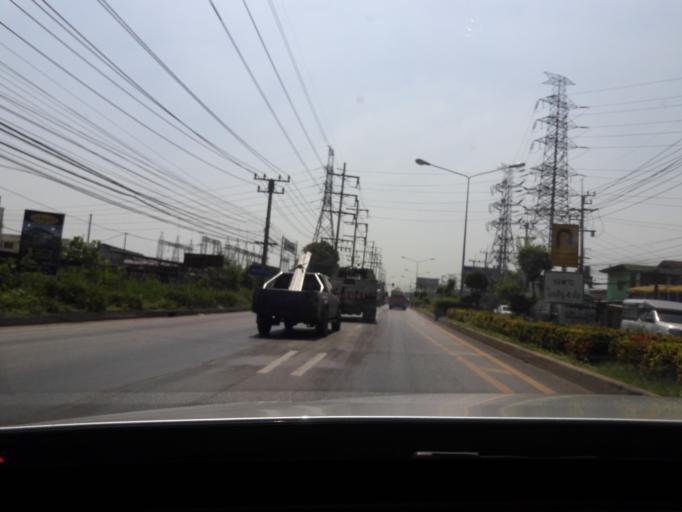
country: TH
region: Samut Sakhon
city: Samut Sakhon
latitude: 13.5947
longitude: 100.2821
